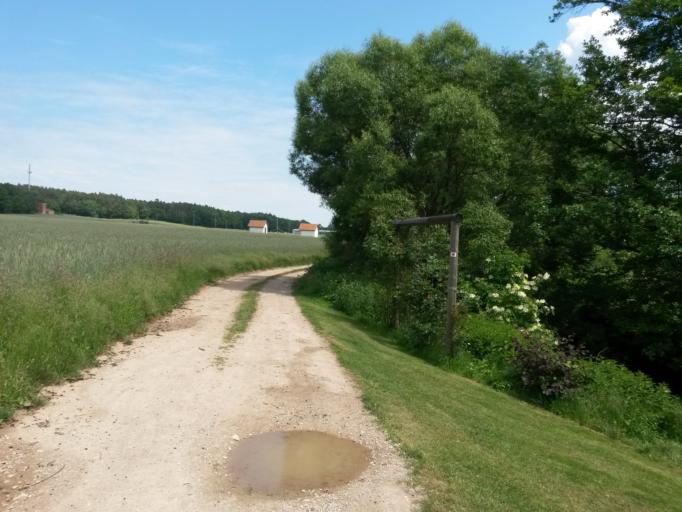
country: DE
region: Bavaria
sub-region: Regierungsbezirk Mittelfranken
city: Rosstal
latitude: 49.4292
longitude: 10.9059
